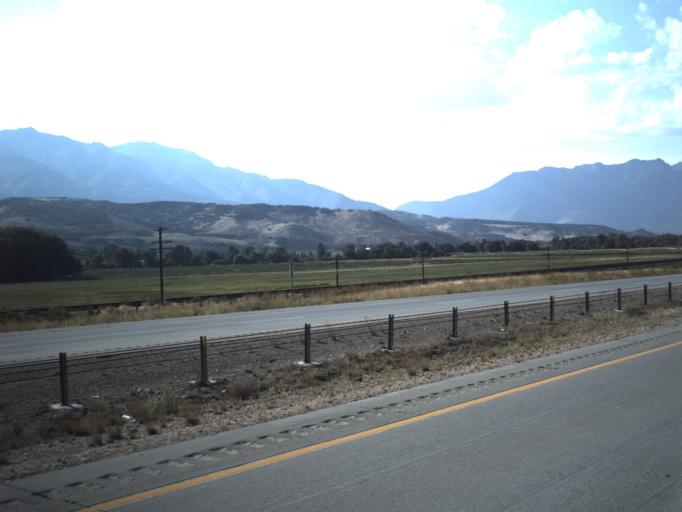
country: US
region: Utah
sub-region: Morgan County
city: Morgan
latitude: 41.0886
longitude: -111.7347
